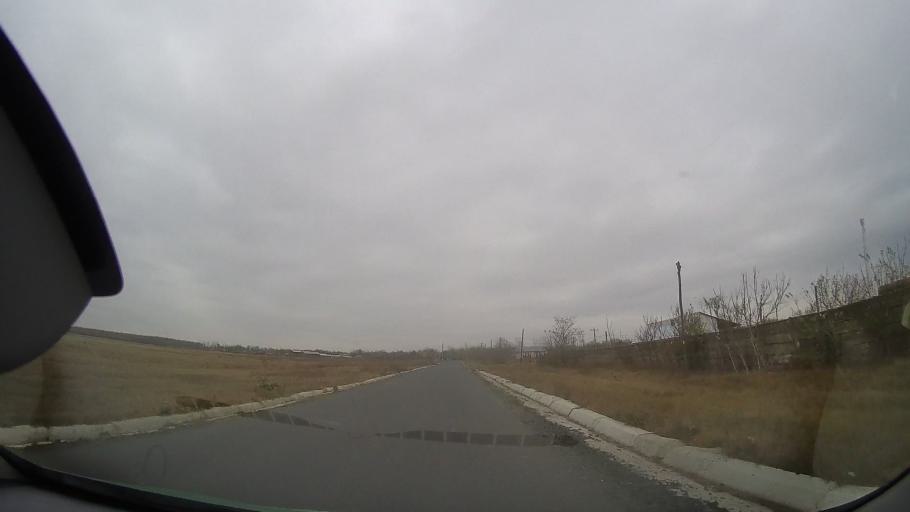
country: RO
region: Braila
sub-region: Comuna Ciocile
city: Ciocile
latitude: 44.8007
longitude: 27.2722
